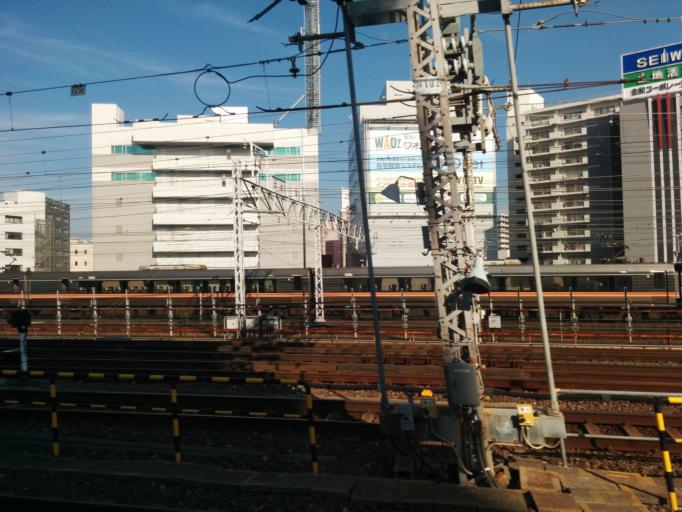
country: JP
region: Aichi
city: Nagoya-shi
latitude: 35.1762
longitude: 136.8786
